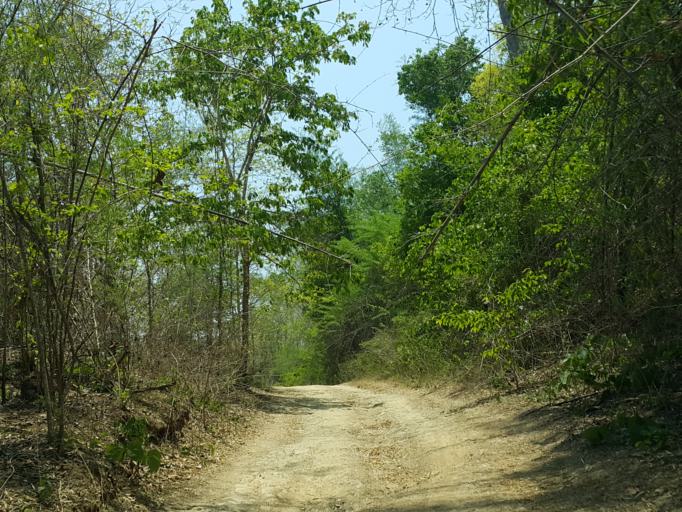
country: TH
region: Kanchanaburi
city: Sai Yok
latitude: 14.2342
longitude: 98.8622
